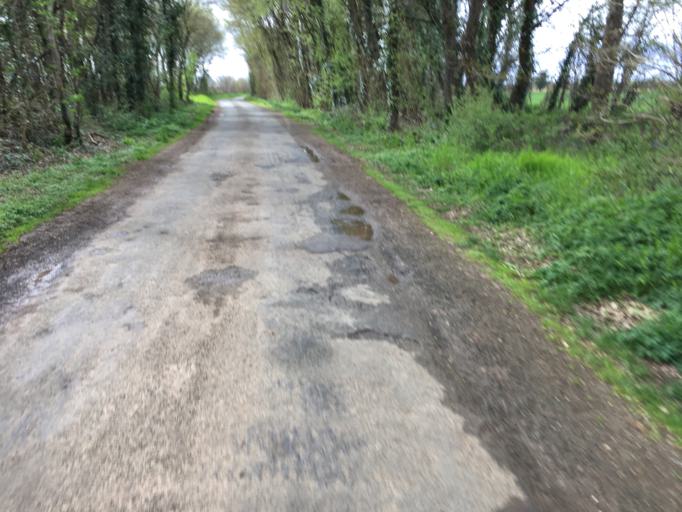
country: FR
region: Poitou-Charentes
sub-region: Departement de la Charente-Maritime
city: Saint-Germain-de-Marencennes
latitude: 46.1131
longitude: -0.8103
